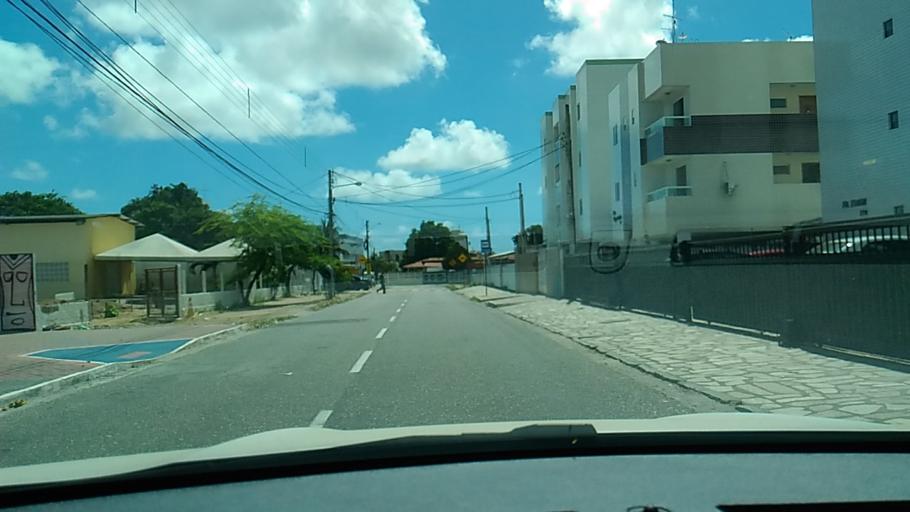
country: BR
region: Paraiba
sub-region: Joao Pessoa
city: Joao Pessoa
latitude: -7.1517
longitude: -34.8491
